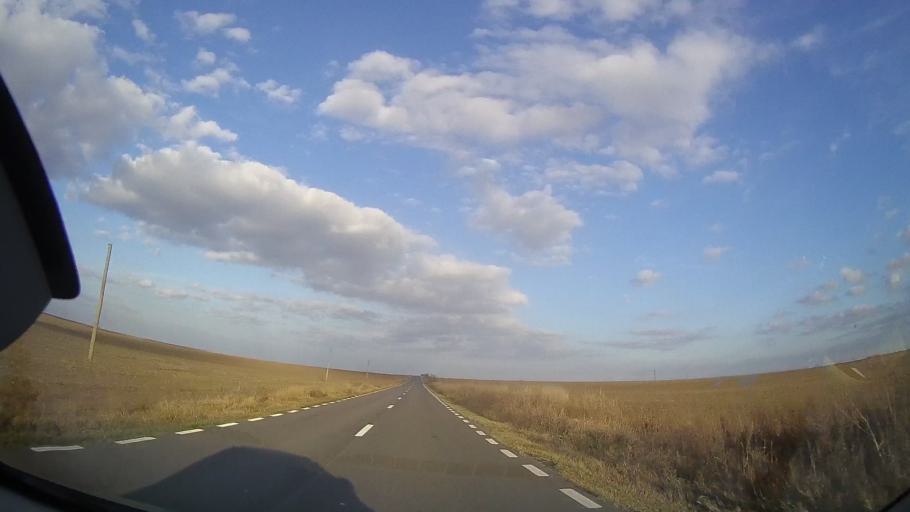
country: RO
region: Constanta
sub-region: Comuna Independenta
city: Independenta
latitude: 43.9450
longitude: 28.0615
